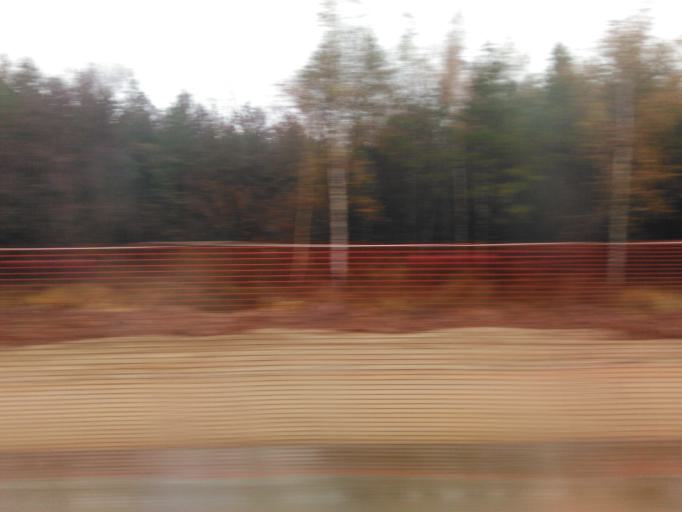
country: RU
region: Tatarstan
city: Sviyazhsk
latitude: 55.7528
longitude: 48.8039
